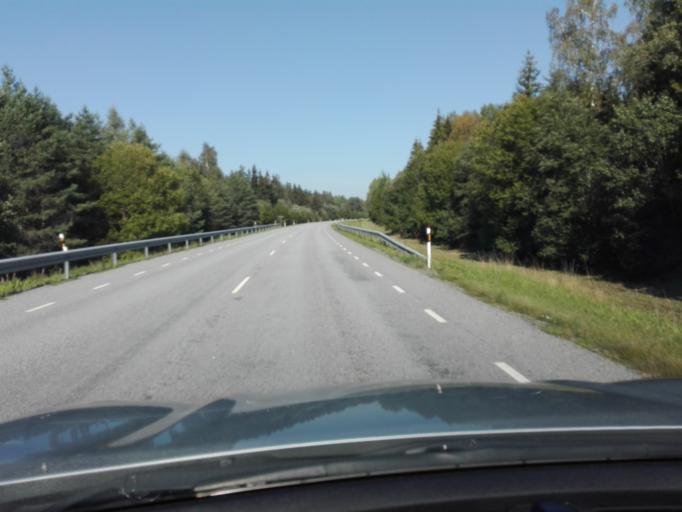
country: EE
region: Raplamaa
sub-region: Rapla vald
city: Rapla
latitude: 59.0053
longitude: 24.7690
